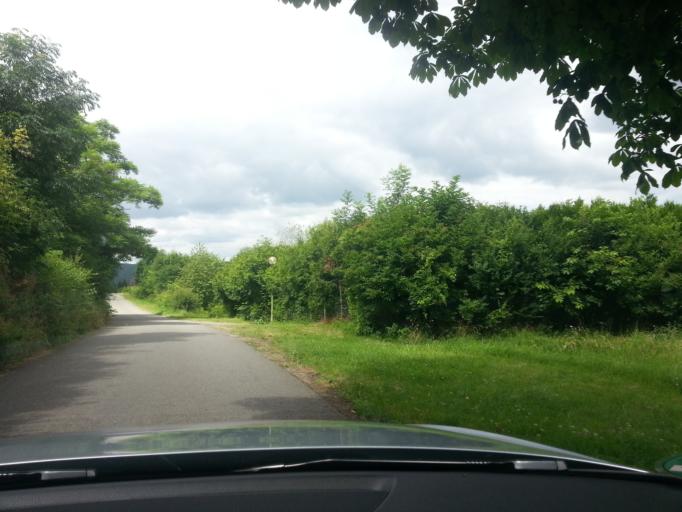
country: LU
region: Grevenmacher
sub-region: Canton de Remich
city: Bous
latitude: 49.5385
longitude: 6.3381
